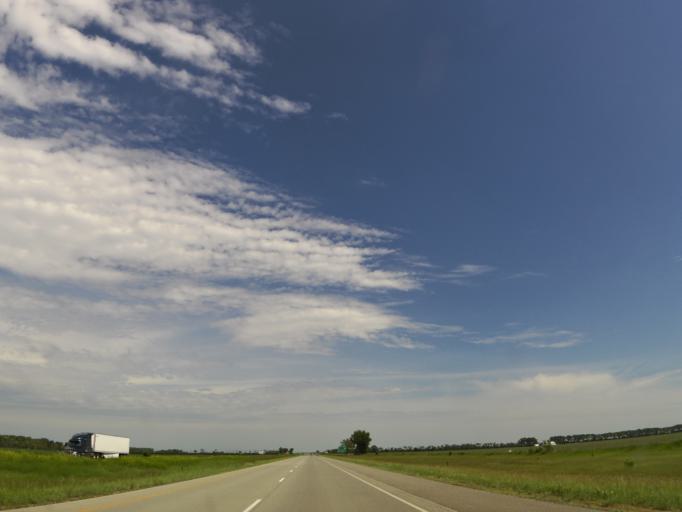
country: US
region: North Dakota
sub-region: Grand Forks County
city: Grand Forks
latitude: 47.7513
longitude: -97.0776
